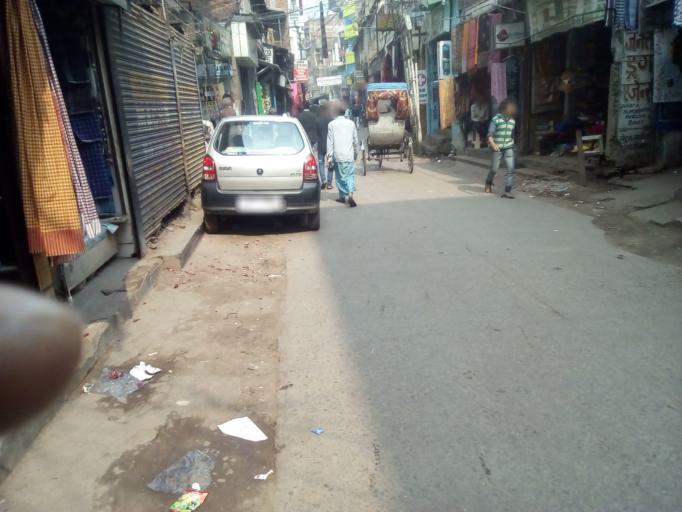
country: IN
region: Bihar
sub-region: Patna
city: Patna
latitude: 25.6179
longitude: 85.1553
